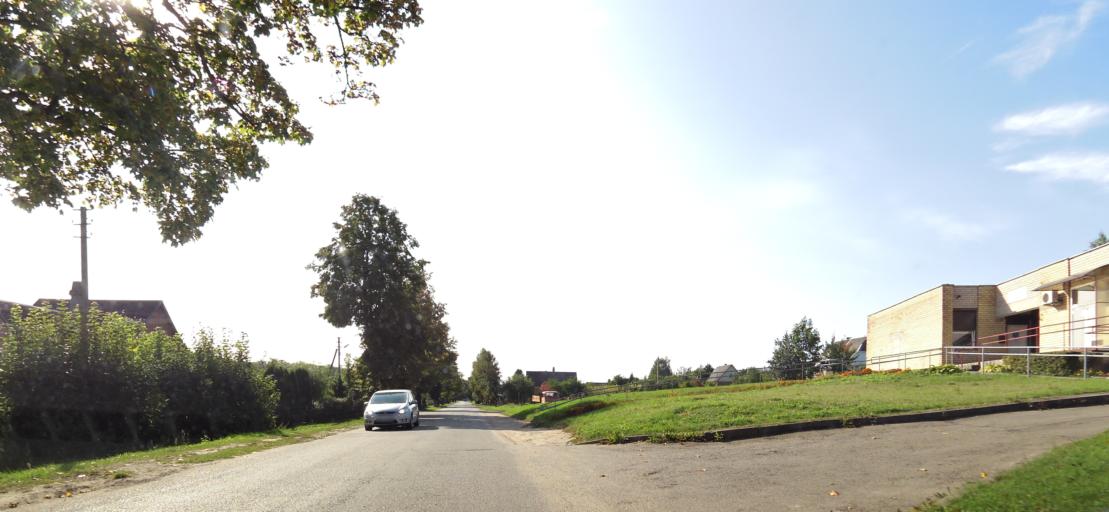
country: LT
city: Salcininkai
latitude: 54.4369
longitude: 25.3071
